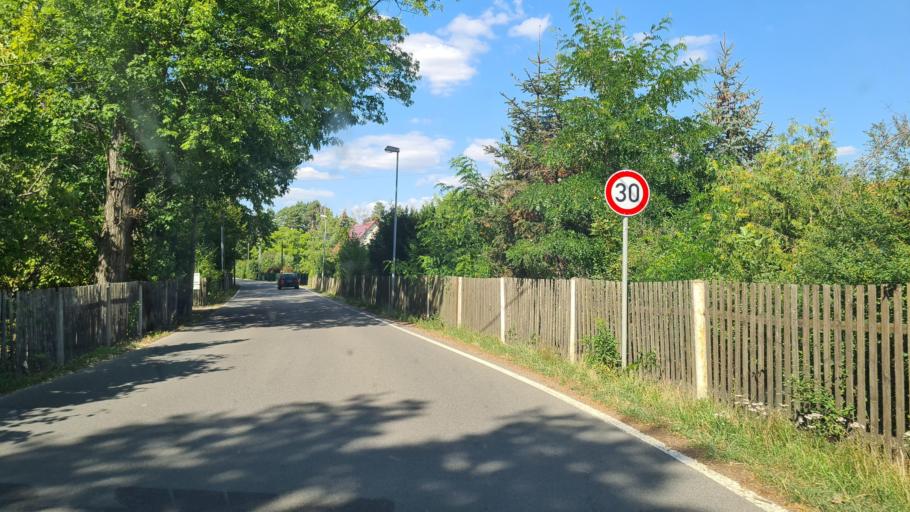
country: DE
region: Saxony
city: Machern
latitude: 51.3661
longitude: 12.6394
